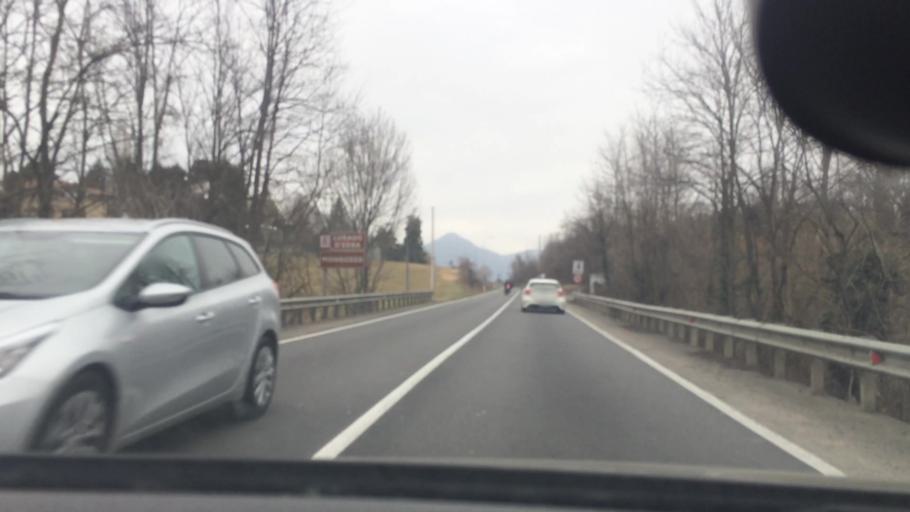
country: IT
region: Lombardy
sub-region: Provincia di Como
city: Nobile-Monguzzo
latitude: 45.7696
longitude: 9.2298
